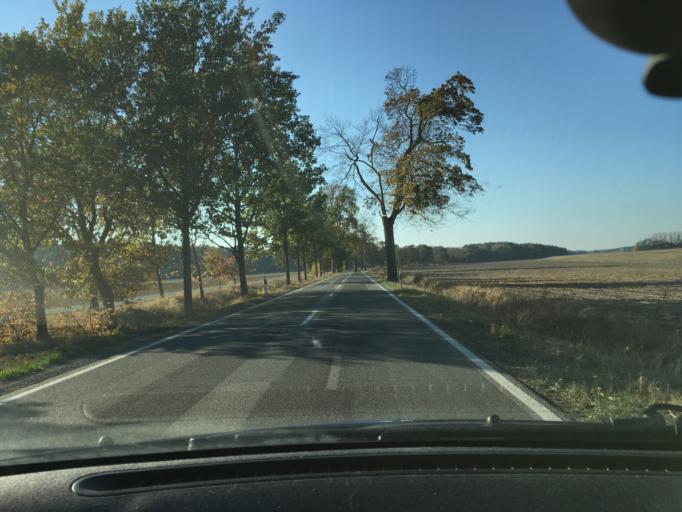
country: DE
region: Mecklenburg-Vorpommern
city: Domitz
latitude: 53.1536
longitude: 11.2219
